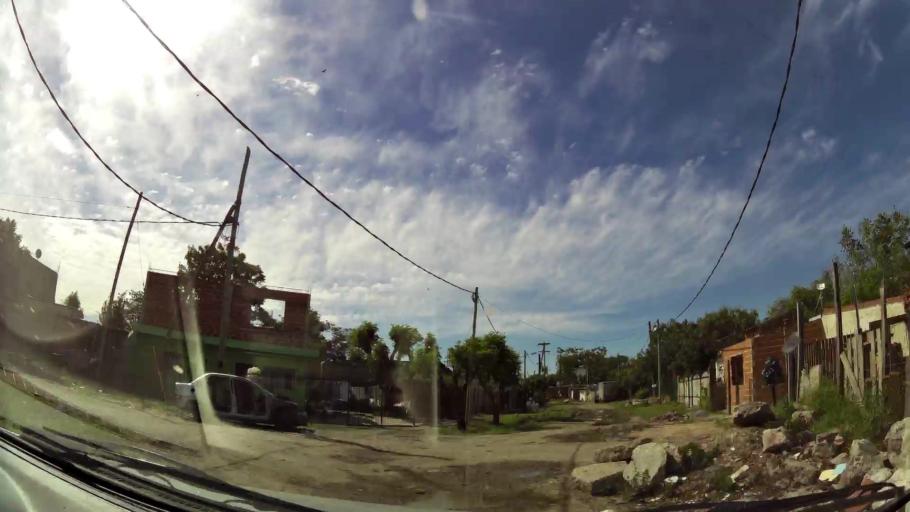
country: AR
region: Buenos Aires
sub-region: Partido de Quilmes
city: Quilmes
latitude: -34.7777
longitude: -58.3021
